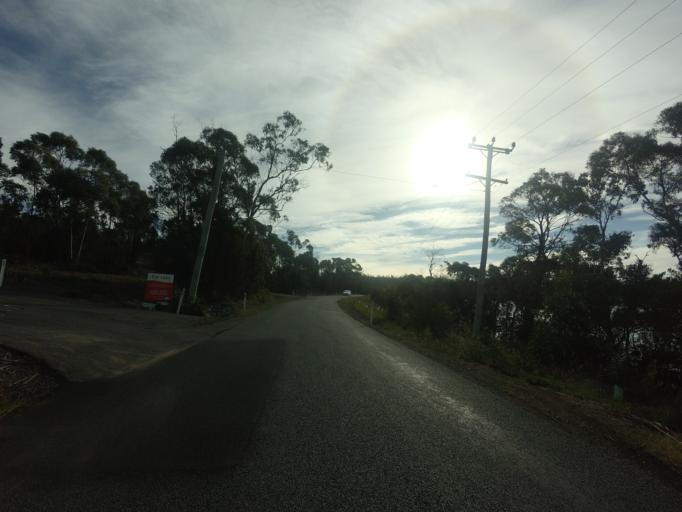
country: AU
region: Tasmania
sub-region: Sorell
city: Sorell
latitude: -42.9471
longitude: 147.8622
